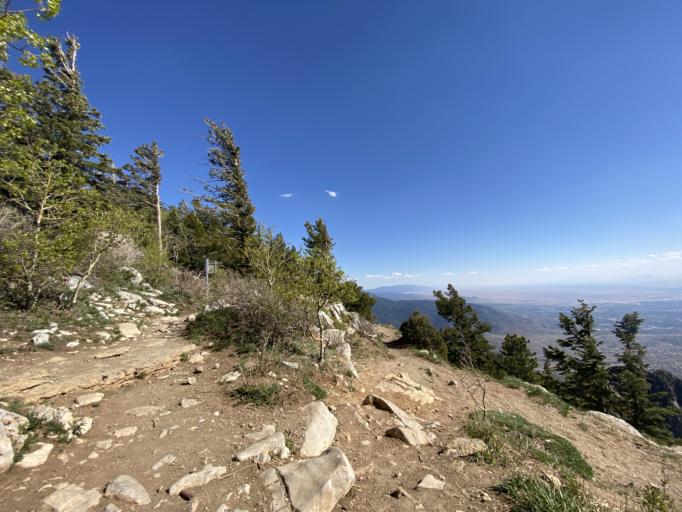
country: US
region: New Mexico
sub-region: Bernalillo County
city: Sandia Heights
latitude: 35.2078
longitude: -106.4474
